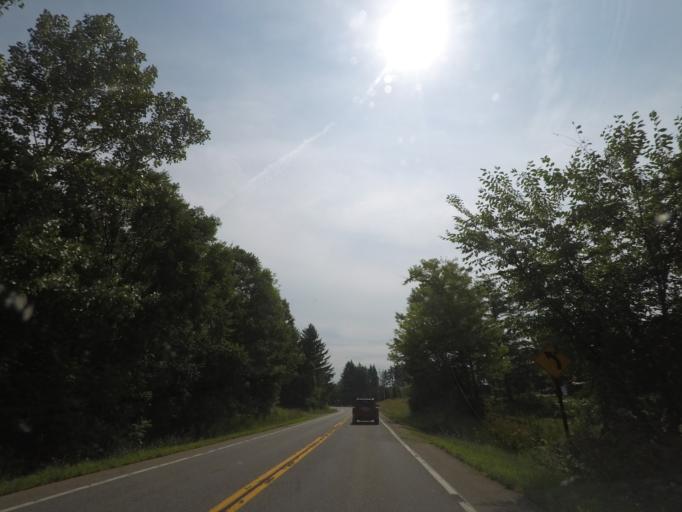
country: US
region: New York
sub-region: Saratoga County
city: Mechanicville
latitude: 42.8937
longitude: -73.7435
